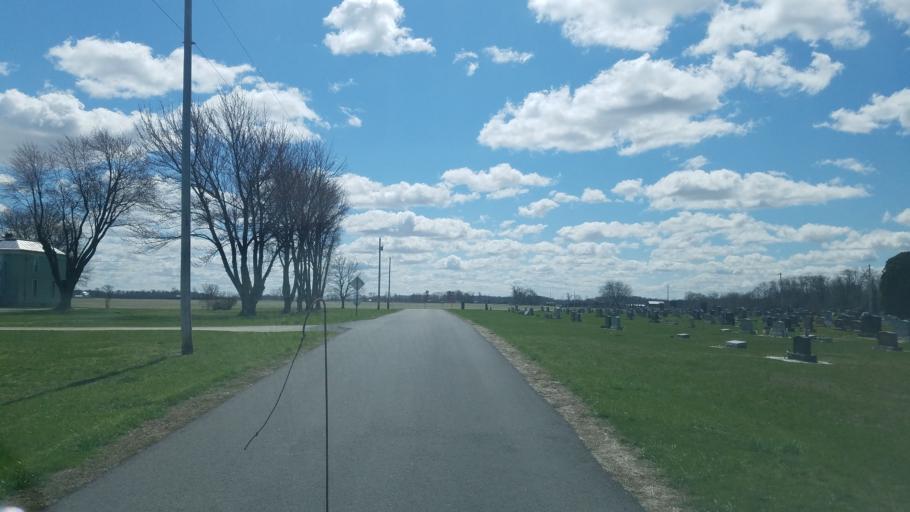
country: US
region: Ohio
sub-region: Hancock County
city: Findlay
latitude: 40.9777
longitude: -83.5345
